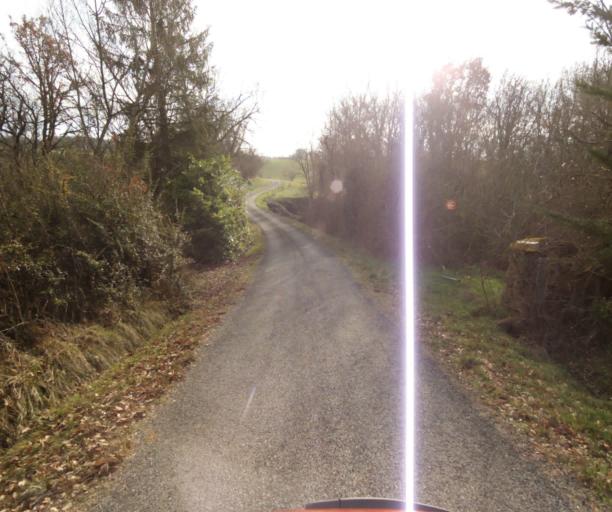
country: FR
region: Languedoc-Roussillon
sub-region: Departement de l'Aude
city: Belpech
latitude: 43.1620
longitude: 1.7381
